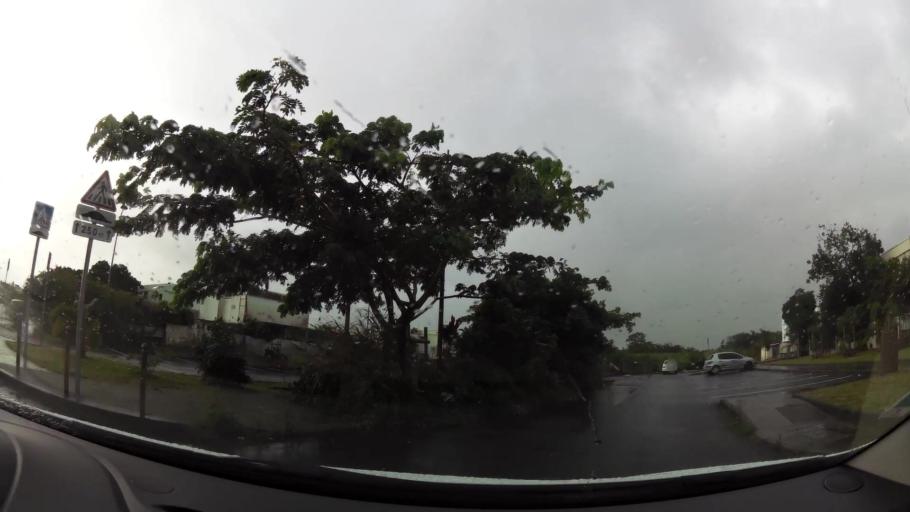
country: RE
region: Reunion
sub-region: Reunion
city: Saint-Andre
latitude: -20.9756
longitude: 55.6606
